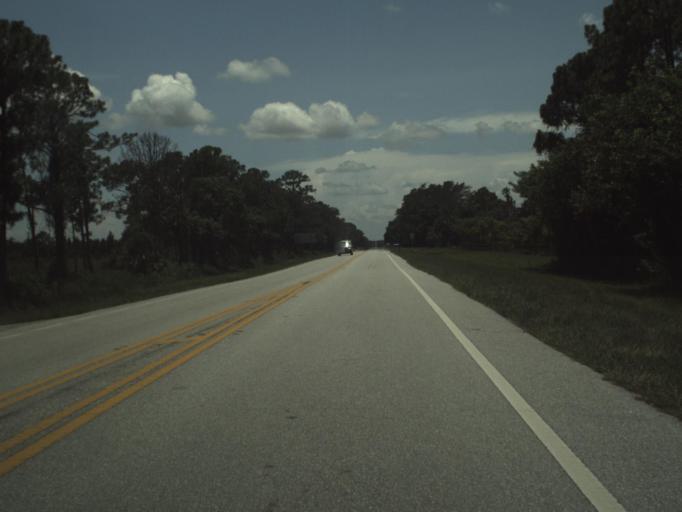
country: US
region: Florida
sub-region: Martin County
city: Palm City
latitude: 27.0859
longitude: -80.2795
